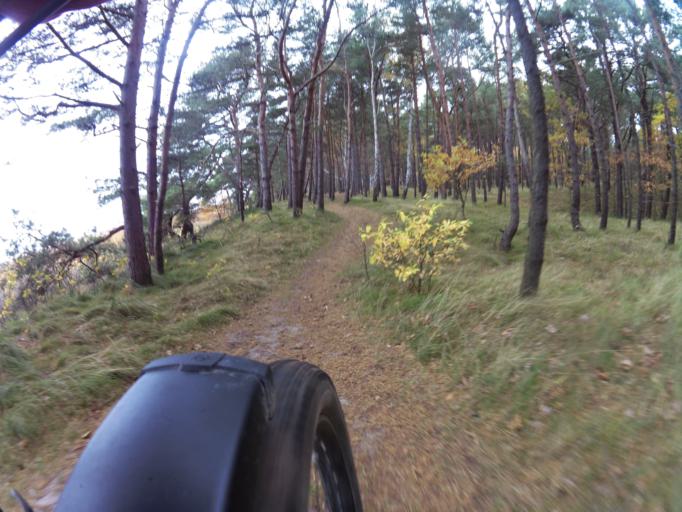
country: PL
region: Pomeranian Voivodeship
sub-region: Powiat pucki
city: Jastarnia
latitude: 54.6892
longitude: 18.6990
